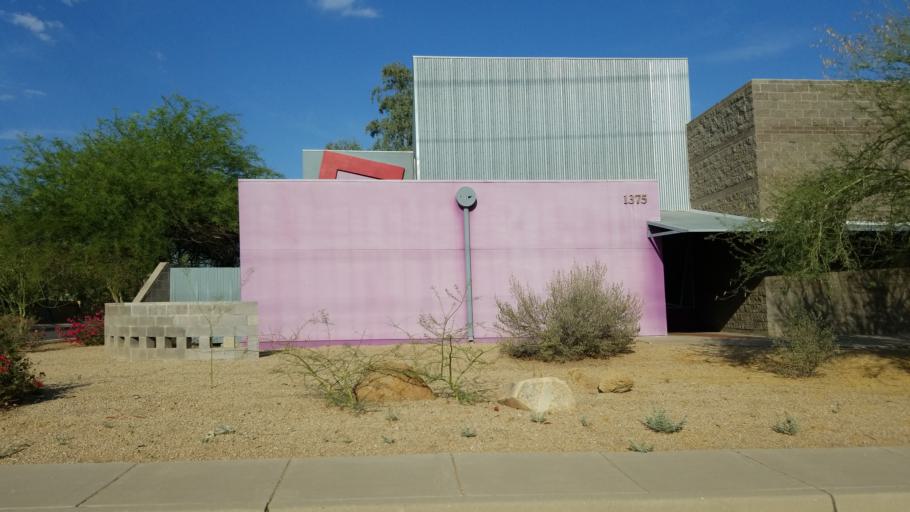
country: US
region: Arizona
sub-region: Maricopa County
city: Tempe
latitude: 33.4437
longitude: -111.9179
